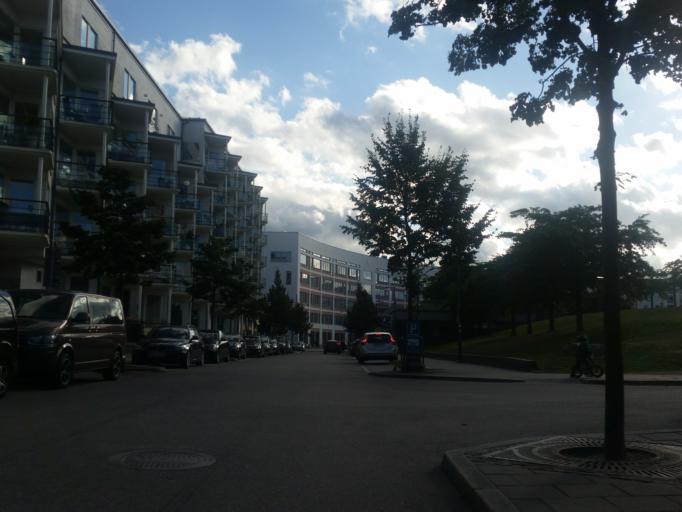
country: SE
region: Stockholm
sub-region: Stockholms Kommun
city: OEstermalm
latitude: 59.3050
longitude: 18.0985
